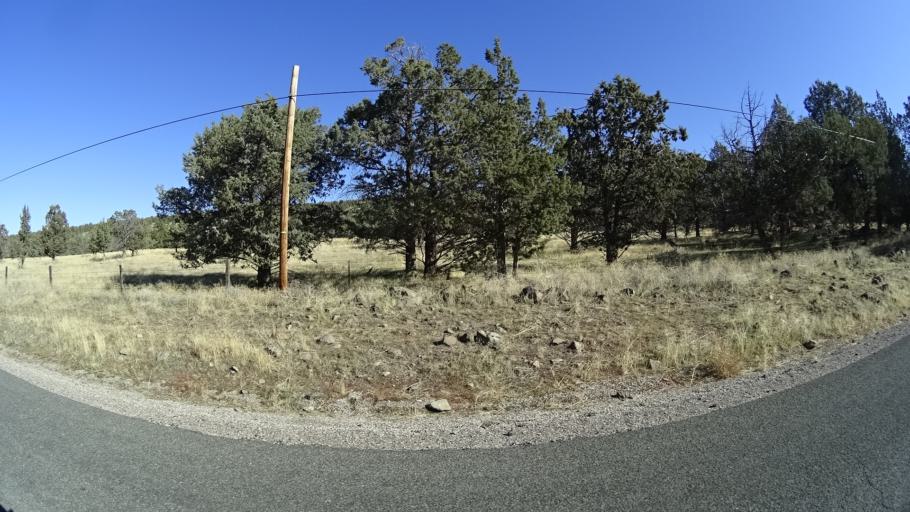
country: US
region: California
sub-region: Siskiyou County
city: Weed
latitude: 41.6244
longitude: -122.3276
